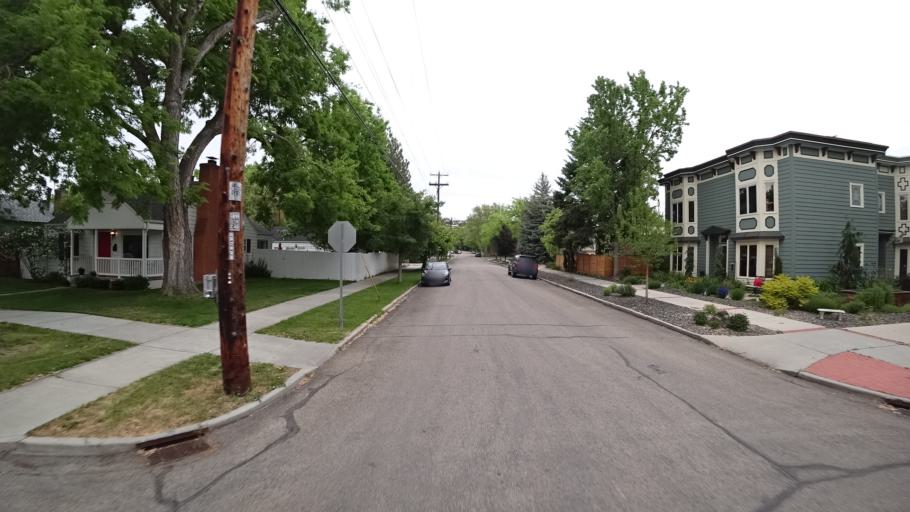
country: US
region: Idaho
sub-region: Ada County
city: Boise
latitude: 43.6096
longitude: -116.1806
